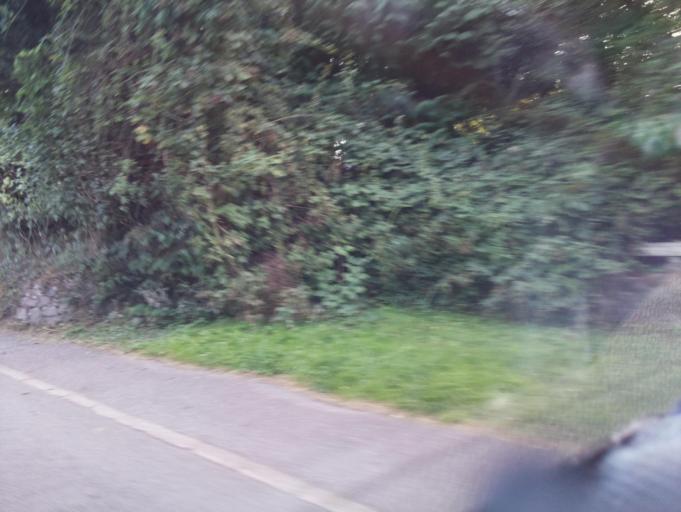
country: GB
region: England
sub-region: Devon
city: Tiverton
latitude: 50.8893
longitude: -3.4966
